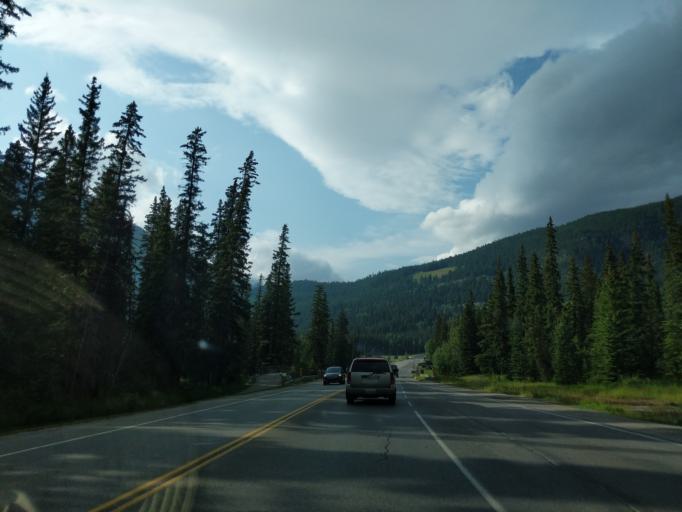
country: CA
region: Alberta
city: Banff
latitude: 51.1831
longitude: -115.5804
